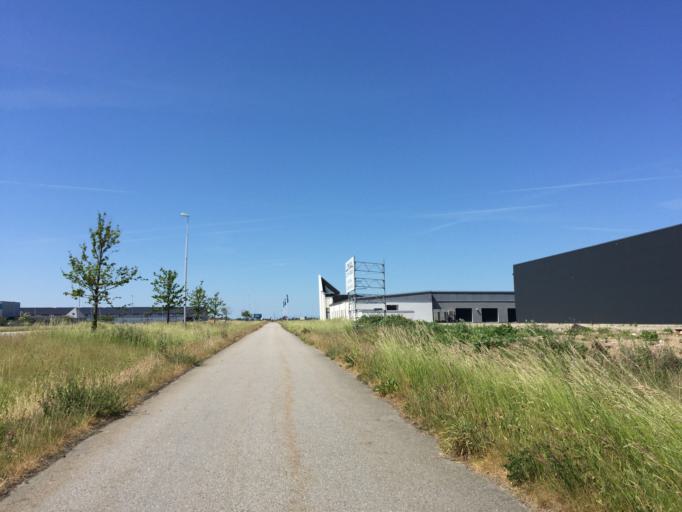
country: SE
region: Skane
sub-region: Trelleborgs Kommun
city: Trelleborg
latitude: 55.3855
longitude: 13.1158
